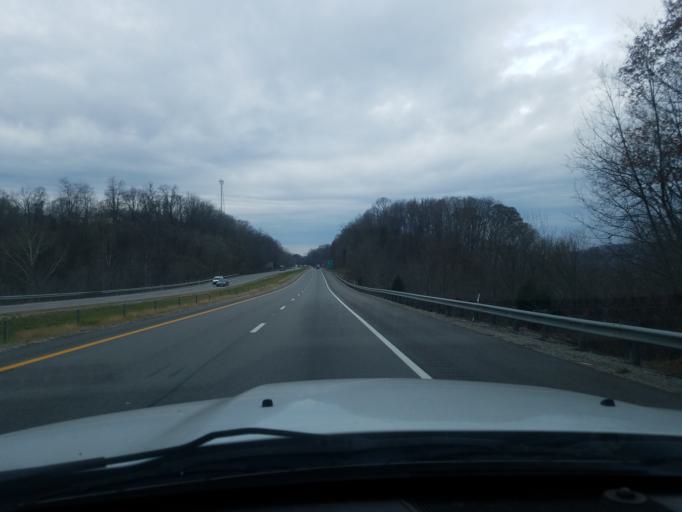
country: US
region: Ohio
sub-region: Lawrence County
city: Burlington
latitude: 38.3948
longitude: -82.5280
